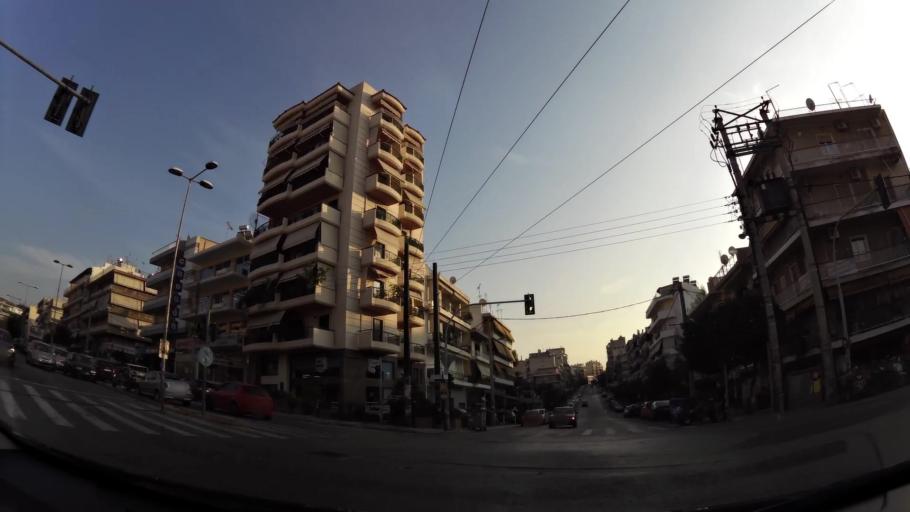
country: GR
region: Attica
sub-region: Nomarchia Athinas
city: Galatsi
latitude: 38.0199
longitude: 23.7531
